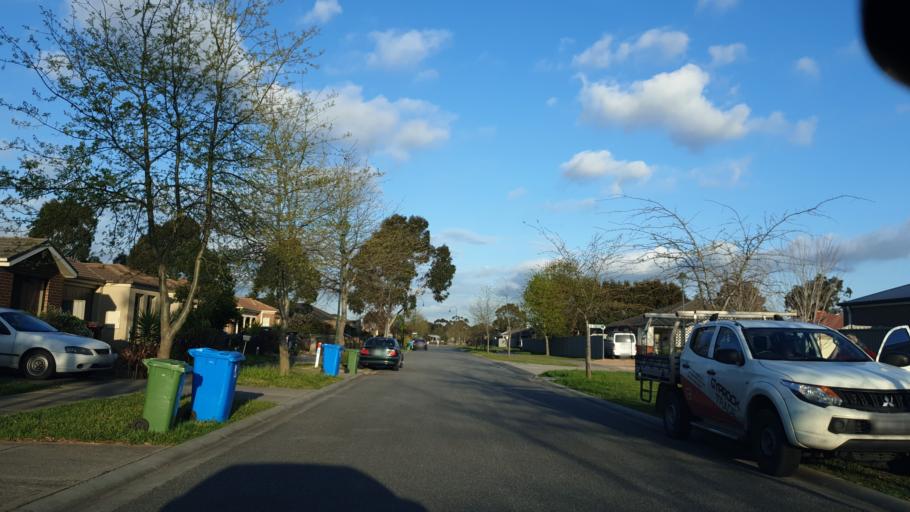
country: AU
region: Victoria
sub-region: Casey
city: Cranbourne East
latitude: -38.1111
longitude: 145.3019
